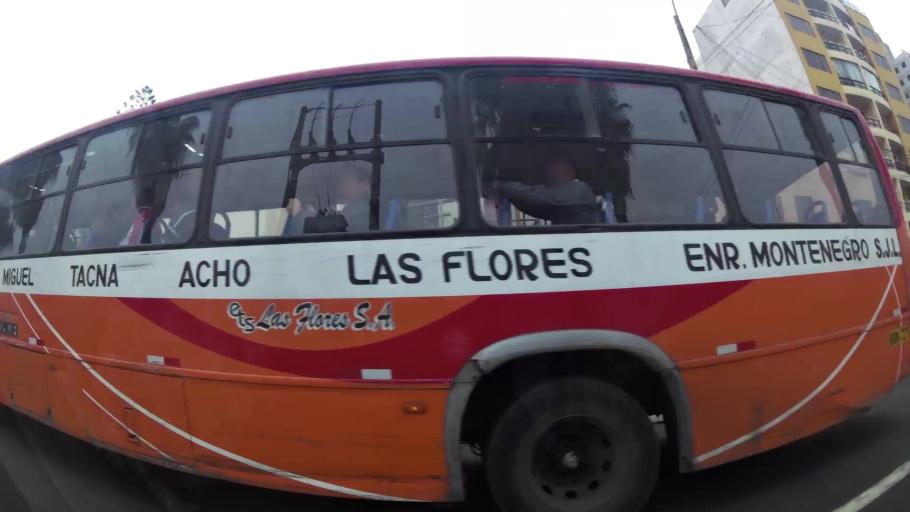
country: PE
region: Lima
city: Lima
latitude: -12.0690
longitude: -77.0614
